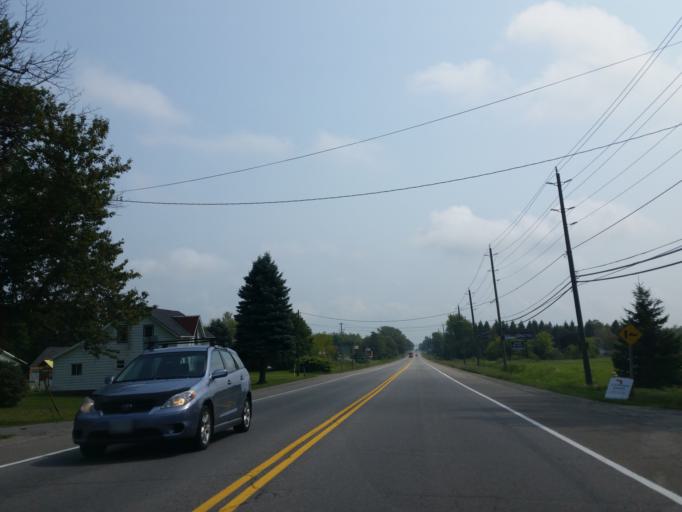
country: CA
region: Ontario
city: Brockville
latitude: 44.6161
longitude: -75.7505
